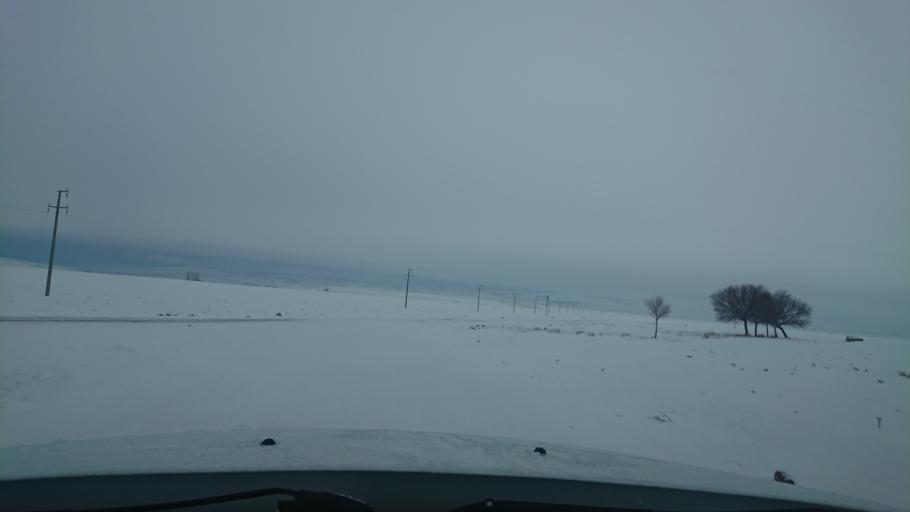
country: TR
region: Aksaray
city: Agacoren
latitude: 38.7212
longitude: 33.8665
